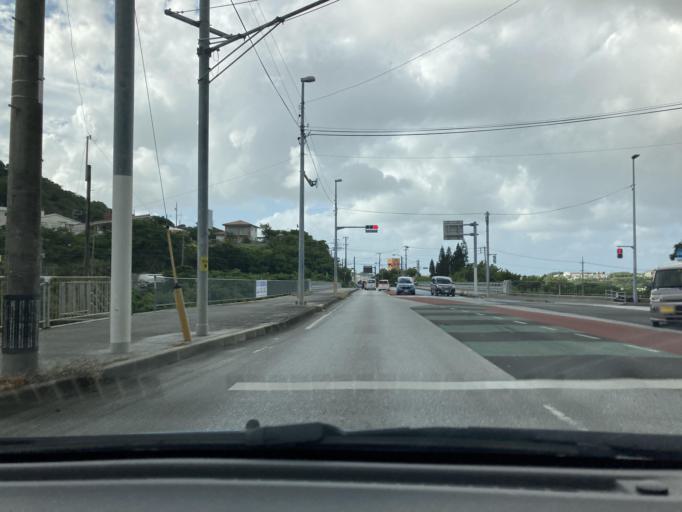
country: JP
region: Okinawa
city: Tomigusuku
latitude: 26.1711
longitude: 127.6917
